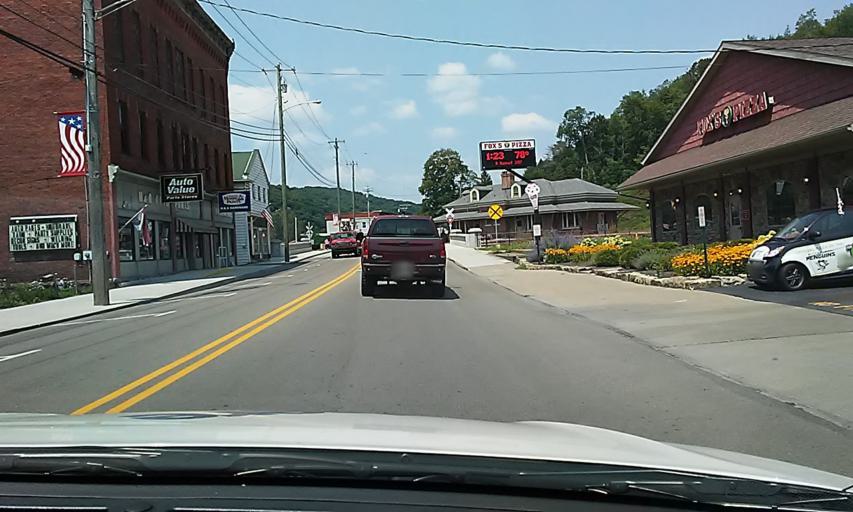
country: US
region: Pennsylvania
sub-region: Elk County
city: Ridgway
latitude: 41.4244
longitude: -78.7310
